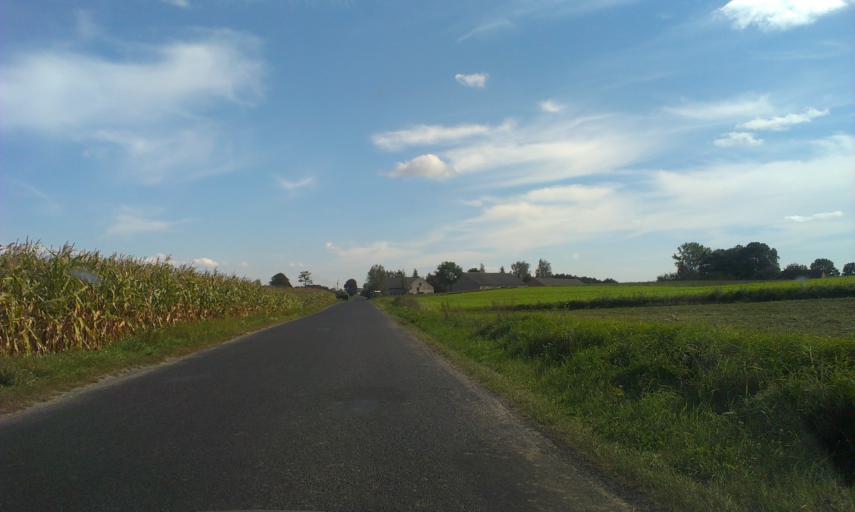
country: PL
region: Greater Poland Voivodeship
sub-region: Powiat pilski
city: Lobzenica
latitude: 53.2792
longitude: 17.1990
